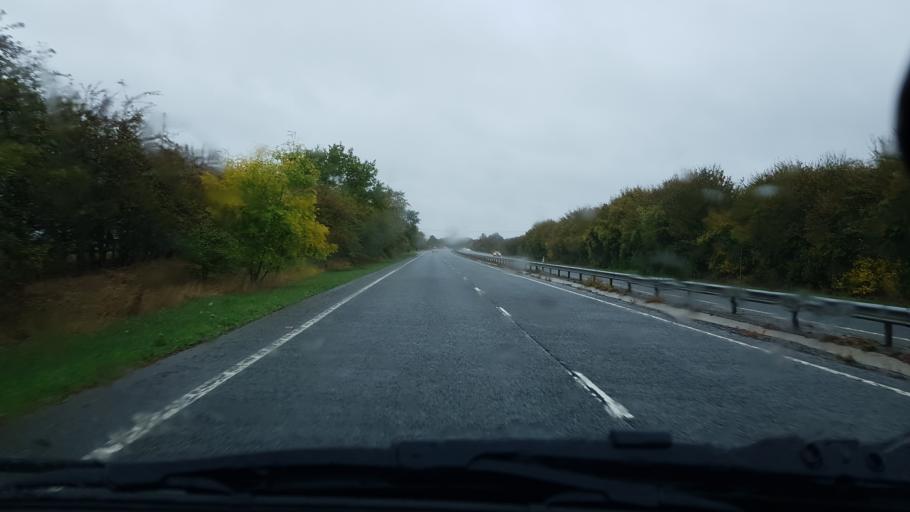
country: GB
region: England
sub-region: Oxfordshire
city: Carterton
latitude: 51.7856
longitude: -1.5687
